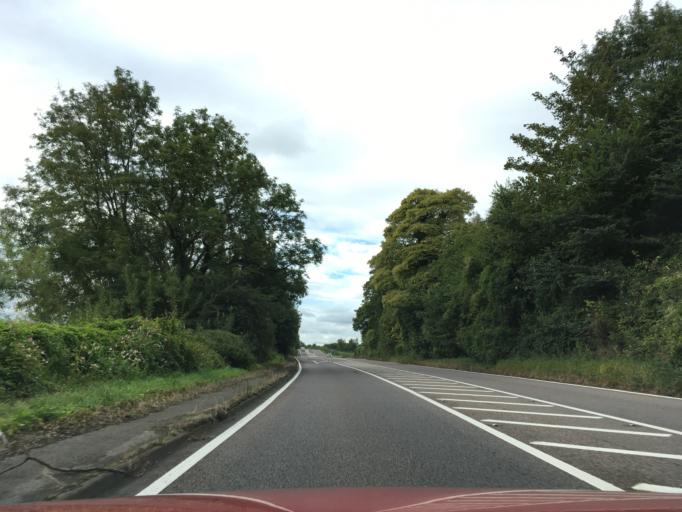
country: GB
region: England
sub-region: Gloucestershire
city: Newent
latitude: 51.8456
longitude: -2.3540
